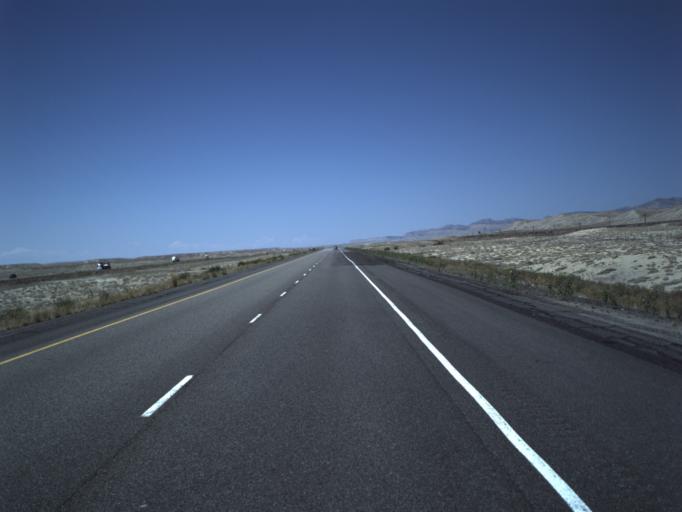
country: US
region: Utah
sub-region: Grand County
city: Moab
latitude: 38.9341
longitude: -109.4444
